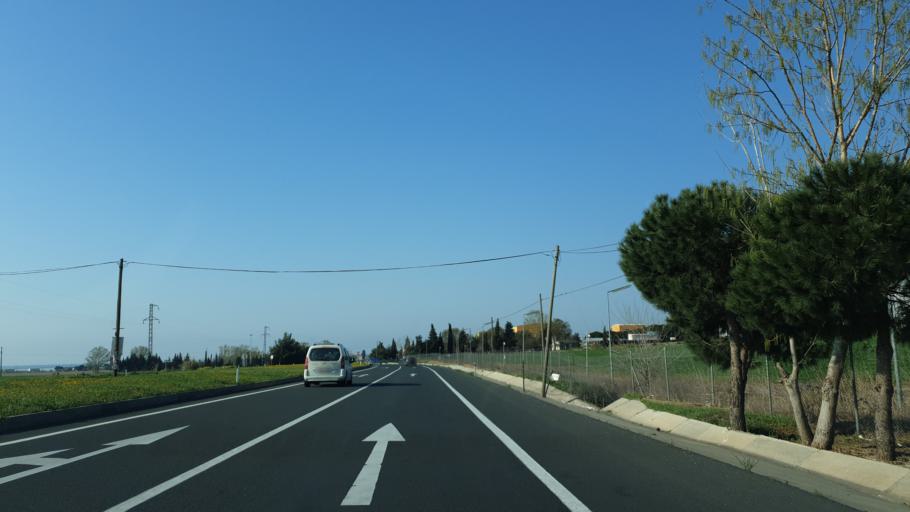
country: TR
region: Tekirdag
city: Corlu
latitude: 41.0247
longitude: 27.7239
